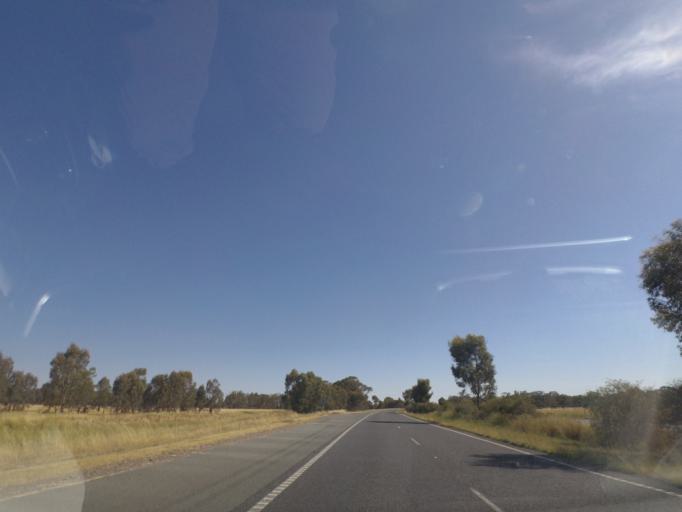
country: AU
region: Victoria
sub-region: Greater Shepparton
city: Shepparton
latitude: -36.6526
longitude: 145.2852
